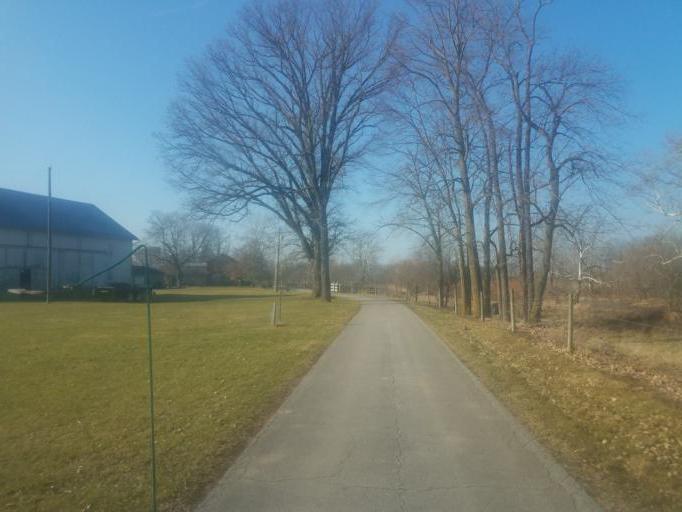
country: US
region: Ohio
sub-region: Seneca County
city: Tiffin
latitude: 41.0619
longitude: -83.0288
